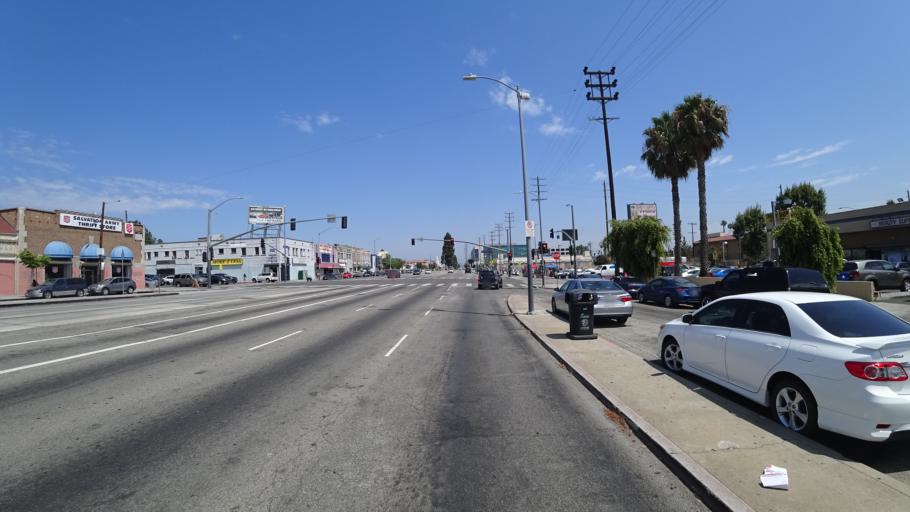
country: US
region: California
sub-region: Los Angeles County
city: Westmont
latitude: 33.9596
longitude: -118.2916
